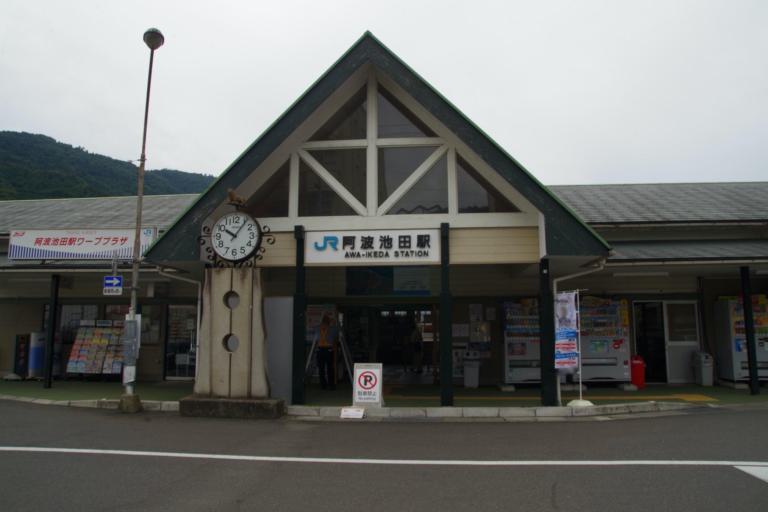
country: JP
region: Tokushima
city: Ikedacho
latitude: 34.0272
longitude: 133.8048
